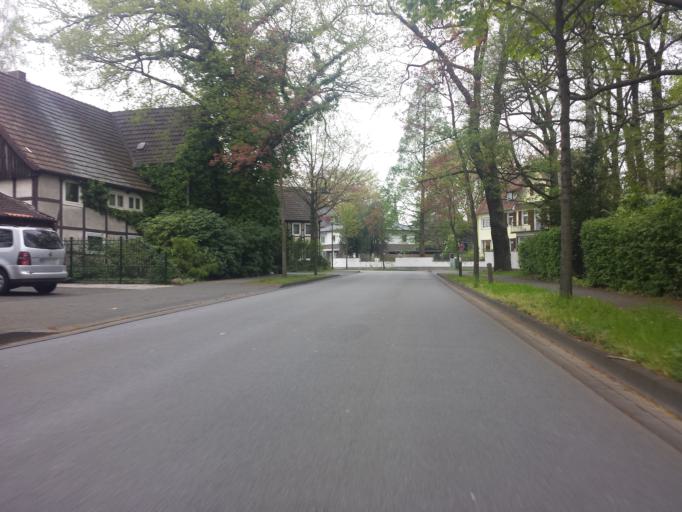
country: DE
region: North Rhine-Westphalia
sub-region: Regierungsbezirk Detmold
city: Guetersloh
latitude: 51.9001
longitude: 8.3815
